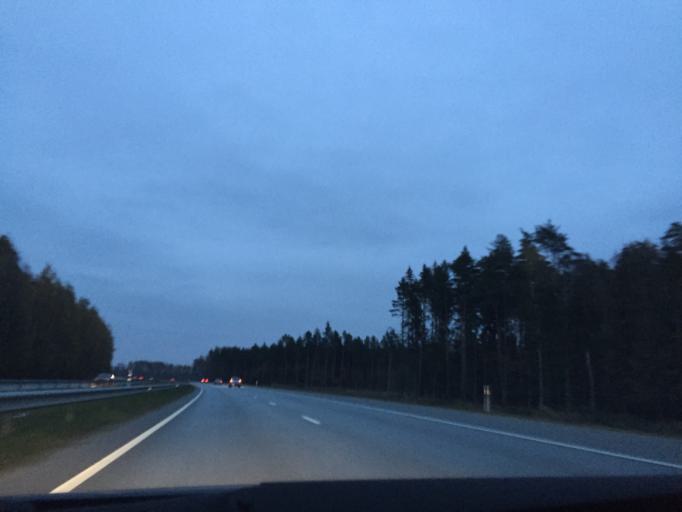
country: LV
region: Marupe
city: Marupe
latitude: 56.8459
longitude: 24.0586
